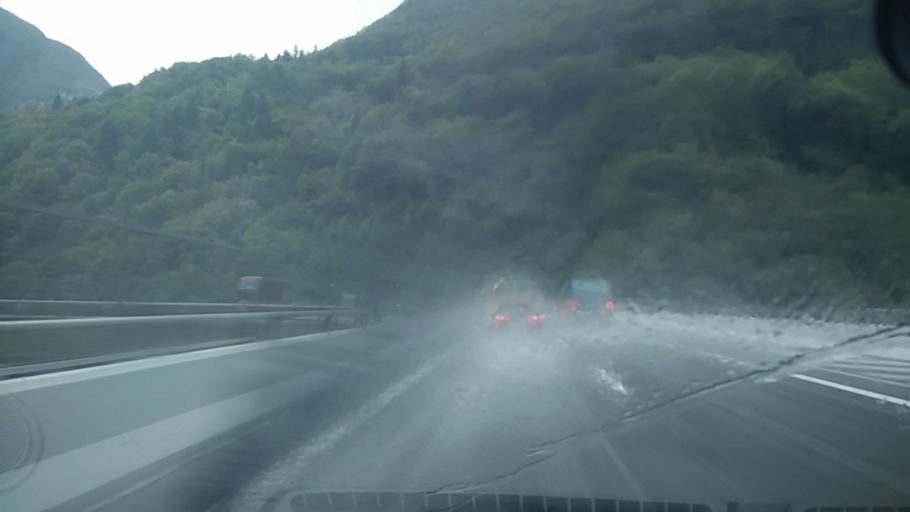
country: IT
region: Friuli Venezia Giulia
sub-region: Provincia di Udine
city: Dogna
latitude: 46.4572
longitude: 13.3039
